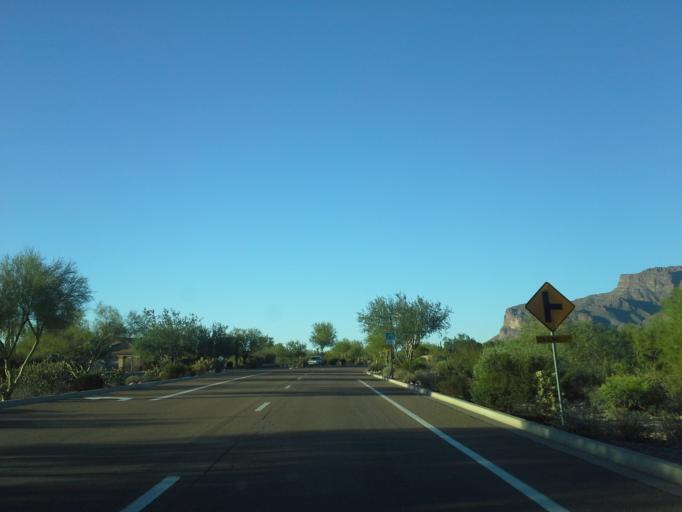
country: US
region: Arizona
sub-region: Pinal County
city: Apache Junction
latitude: 33.3735
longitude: -111.4686
